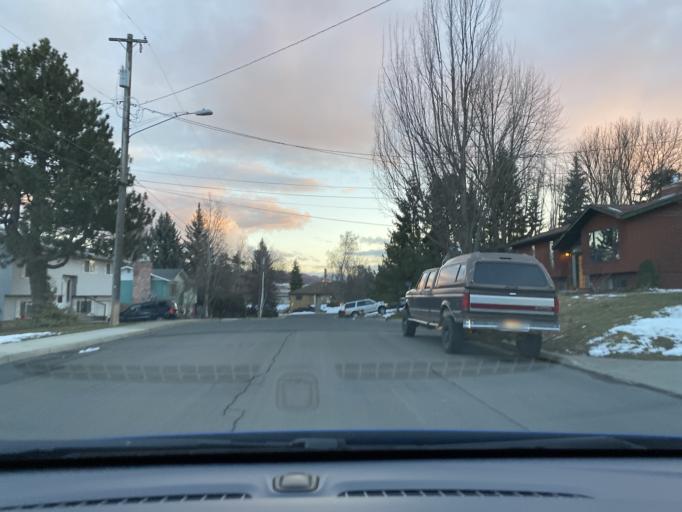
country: US
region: Idaho
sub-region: Latah County
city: Moscow
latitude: 46.7415
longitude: -116.9831
